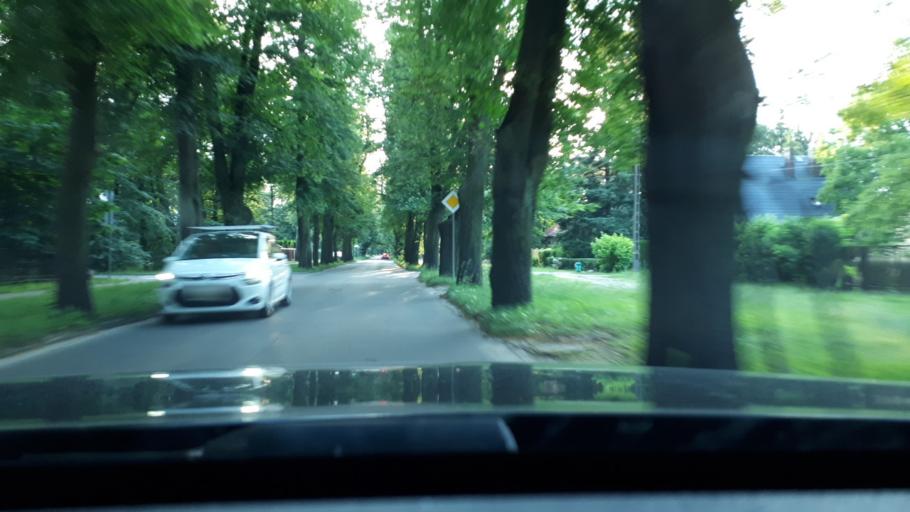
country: PL
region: Masovian Voivodeship
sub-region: Powiat pruszkowski
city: Komorow
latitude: 52.1457
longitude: 20.8225
